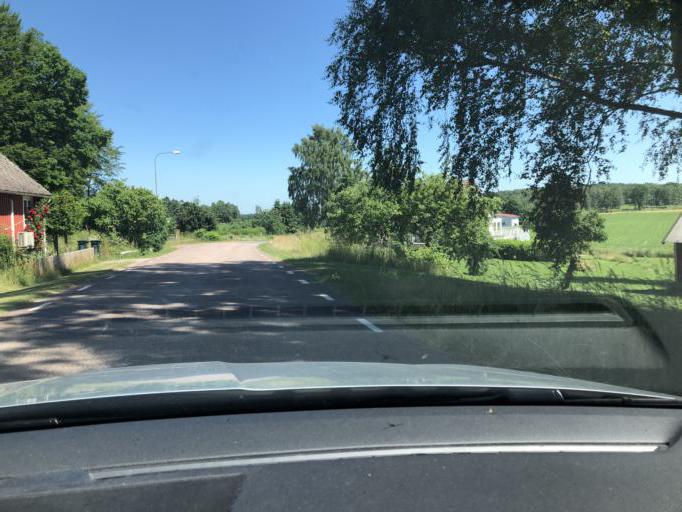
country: SE
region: Blekinge
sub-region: Olofstroms Kommun
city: Jamshog
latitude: 56.1683
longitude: 14.6005
